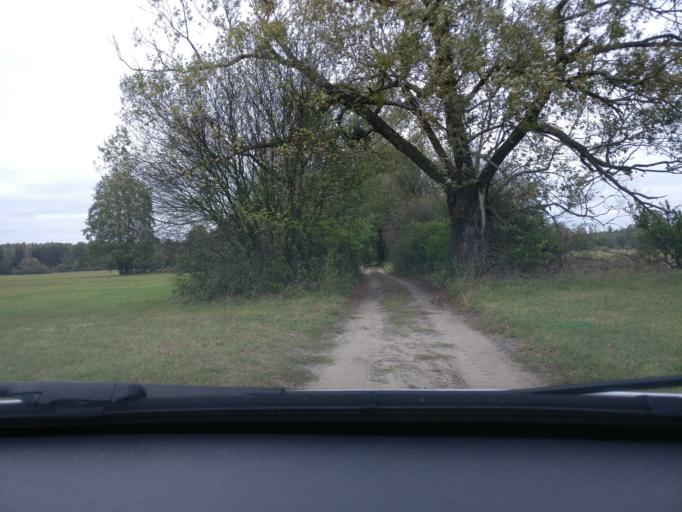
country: PL
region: Masovian Voivodeship
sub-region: Powiat kozienicki
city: Garbatka-Letnisko
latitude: 51.5195
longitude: 21.5998
